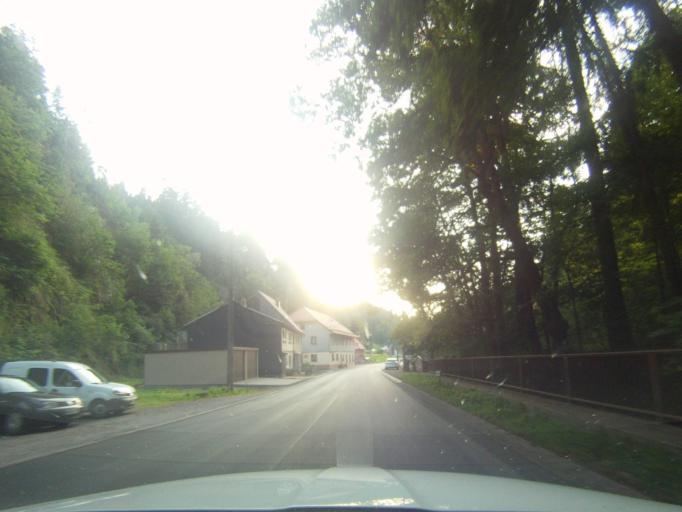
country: DE
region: Thuringia
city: Eisfeld
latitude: 50.4958
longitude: 10.8562
